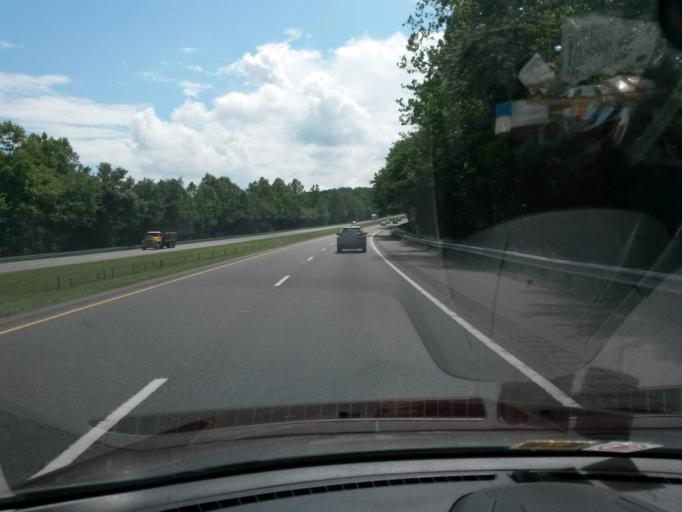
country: US
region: North Carolina
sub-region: Surry County
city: Dobson
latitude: 36.4676
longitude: -80.7576
